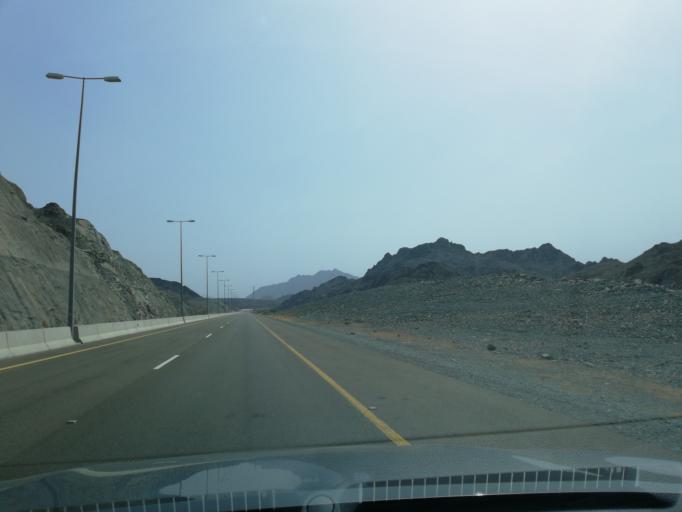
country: OM
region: Al Batinah
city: Al Liwa'
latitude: 24.2667
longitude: 56.3860
